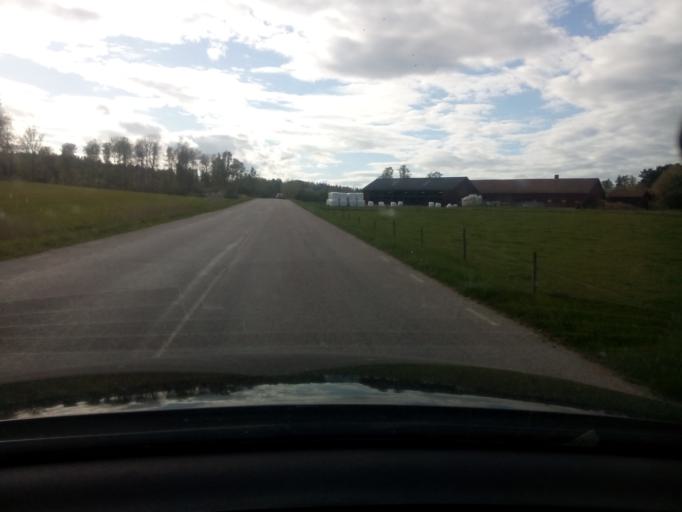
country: SE
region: Soedermanland
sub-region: Nykopings Kommun
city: Stigtomta
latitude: 58.9524
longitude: 16.8650
